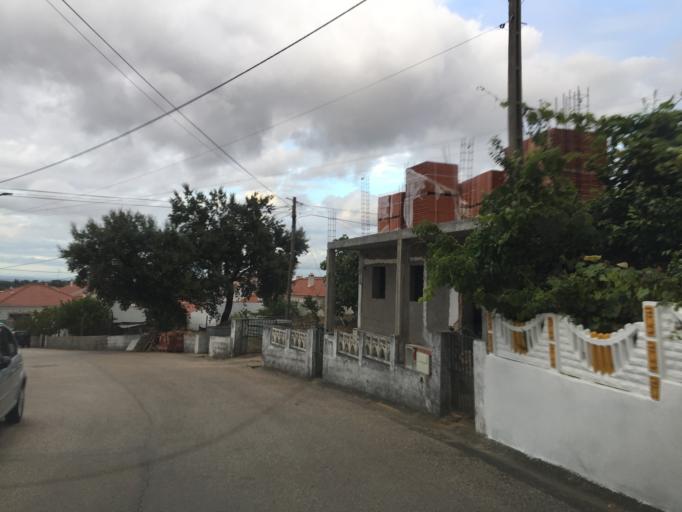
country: PT
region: Portalegre
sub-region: Marvao
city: Marvao
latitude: 39.4111
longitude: -7.3490
